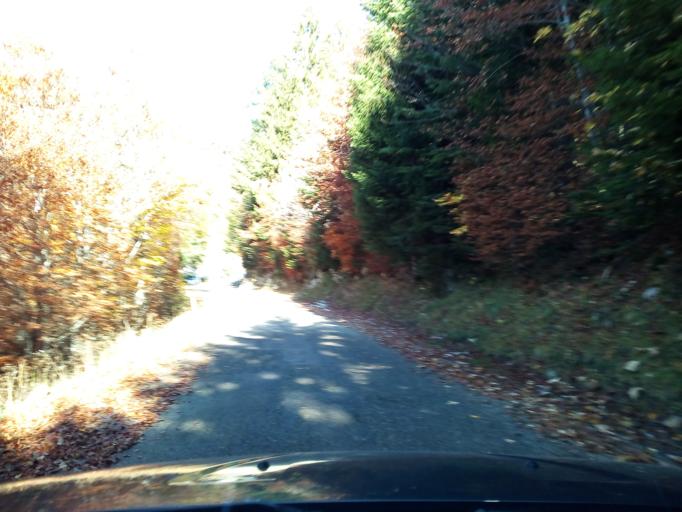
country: FR
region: Rhone-Alpes
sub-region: Departement de l'Isere
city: Bernin
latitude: 45.3017
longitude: 5.8353
